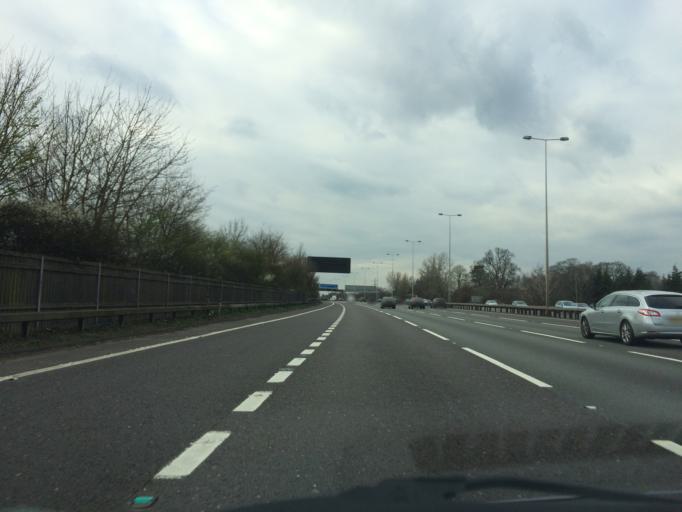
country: GB
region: England
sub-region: Surrey
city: Chertsey
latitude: 51.3808
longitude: -0.5138
